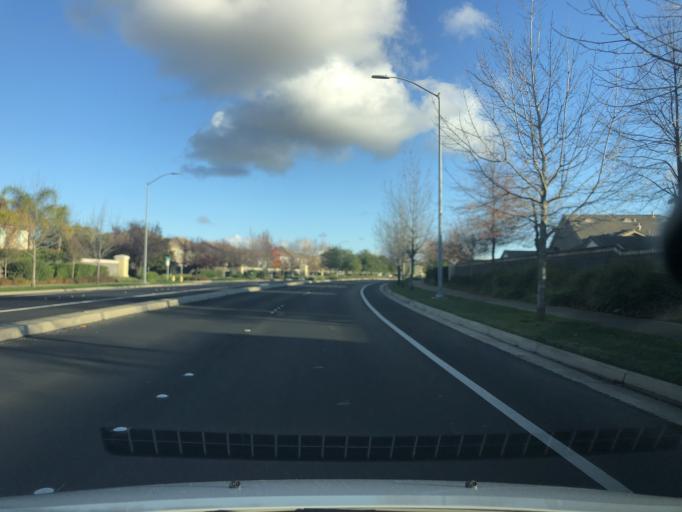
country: US
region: California
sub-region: Sacramento County
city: Antelope
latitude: 38.7752
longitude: -121.3755
